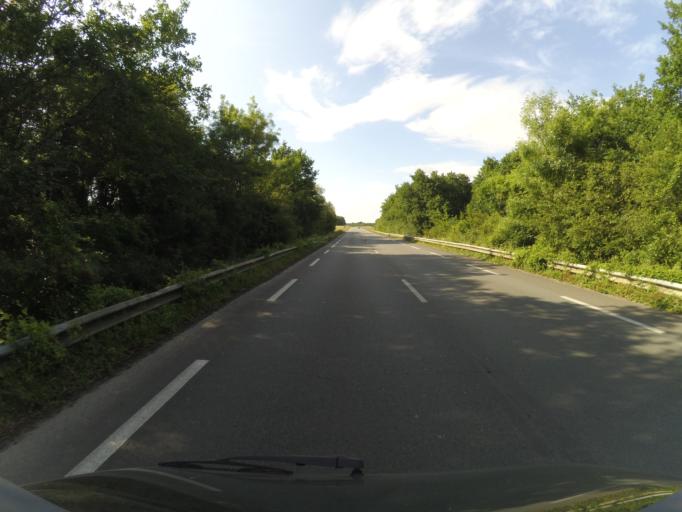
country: FR
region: Poitou-Charentes
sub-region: Departement de la Charente-Maritime
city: Saint-Agnant
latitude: 45.8292
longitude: -0.9363
